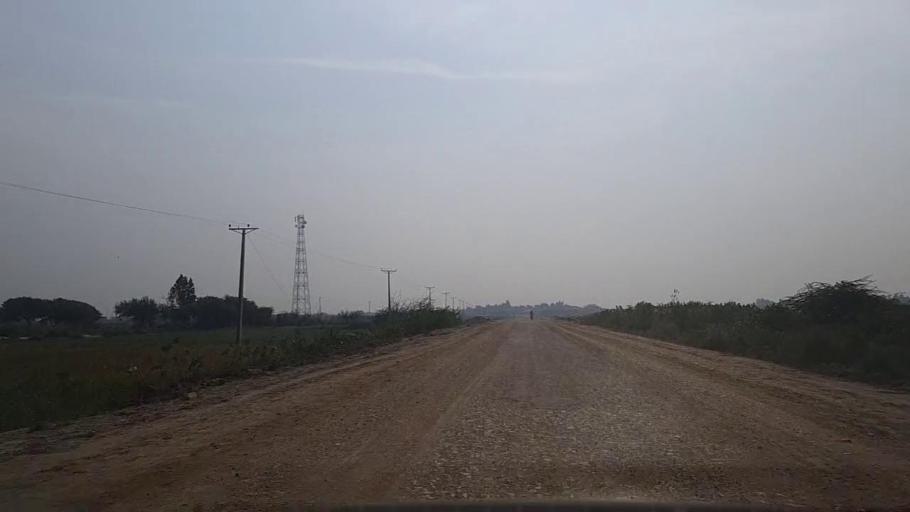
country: PK
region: Sindh
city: Mirpur Sakro
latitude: 24.4075
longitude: 67.7440
